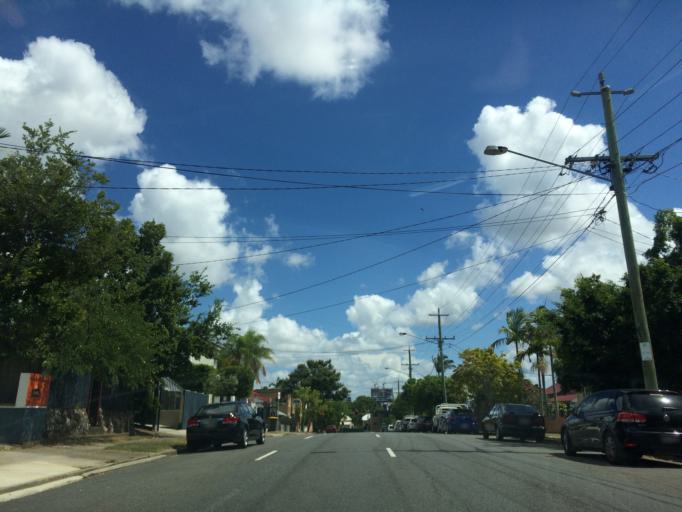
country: AU
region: Queensland
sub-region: Brisbane
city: Woolloongabba
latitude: -27.4839
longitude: 153.0432
